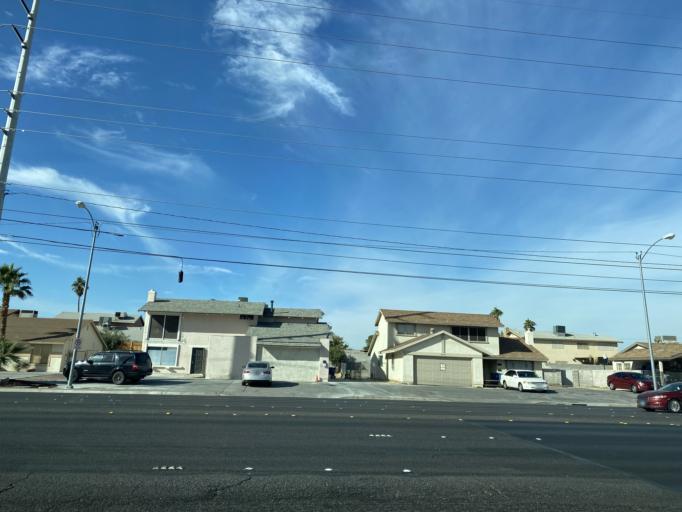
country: US
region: Nevada
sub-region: Clark County
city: Paradise
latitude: 36.0881
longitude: -115.1187
